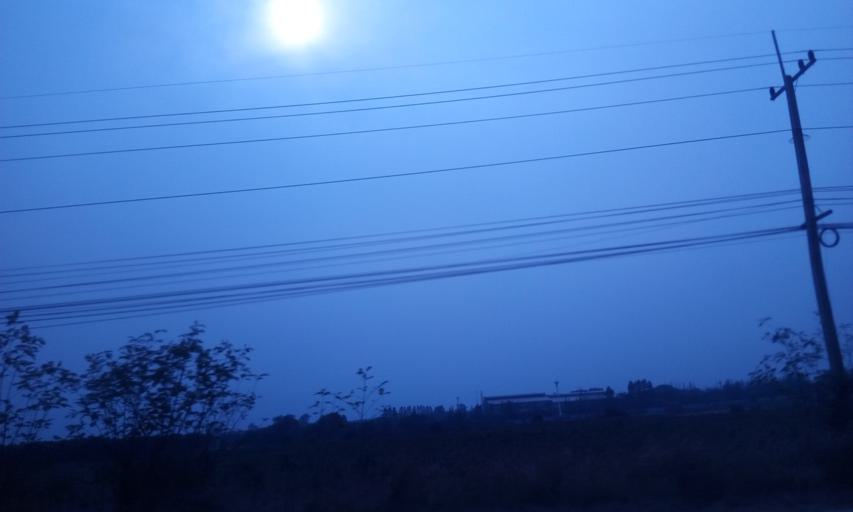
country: TH
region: Chachoengsao
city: Plaeng Yao
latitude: 13.5368
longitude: 101.2629
